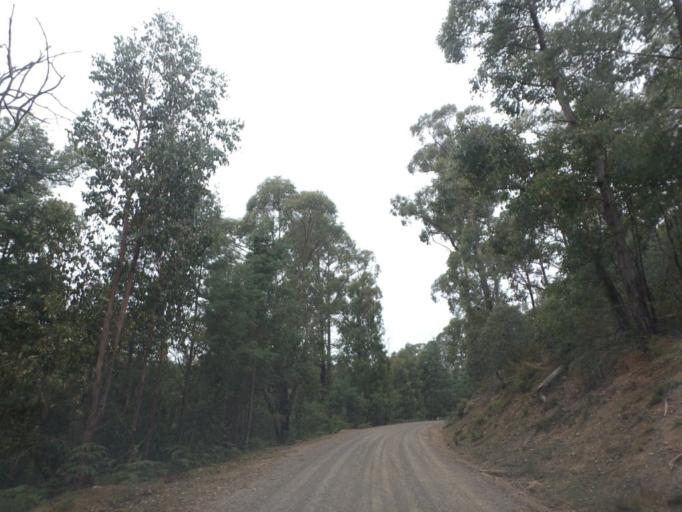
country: AU
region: Victoria
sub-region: Yarra Ranges
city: Healesville
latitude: -37.4219
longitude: 145.5785
